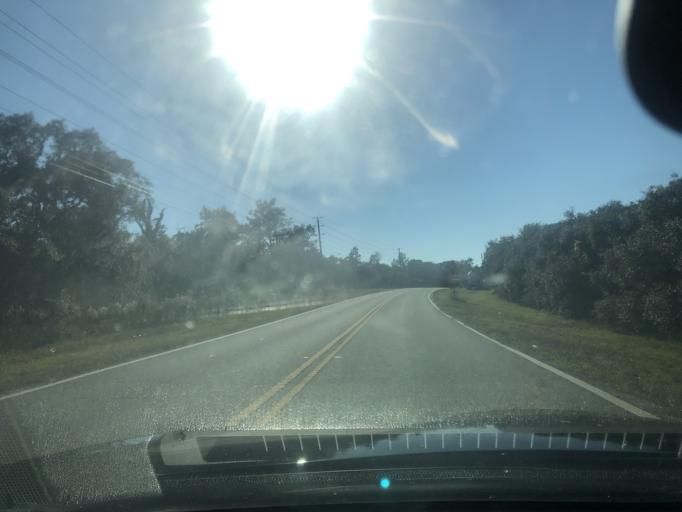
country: US
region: Florida
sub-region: Citrus County
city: Homosassa Springs
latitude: 28.8203
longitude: -82.5325
